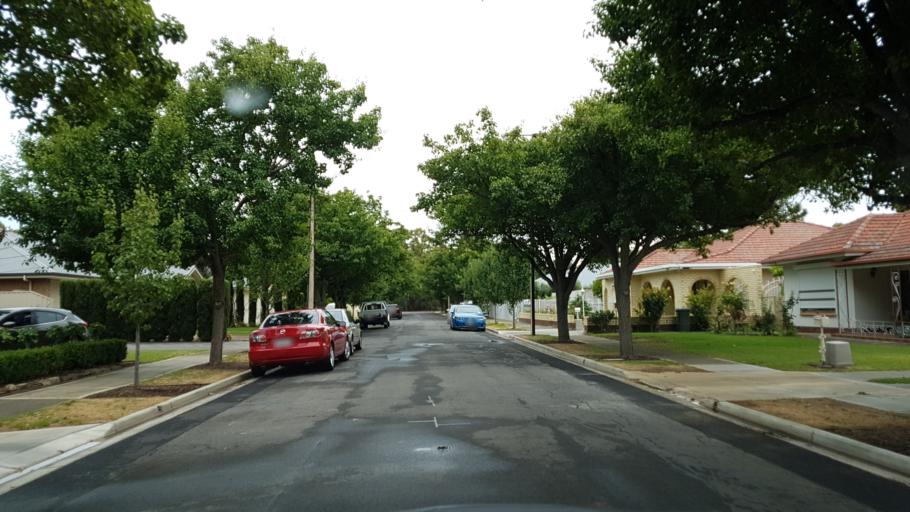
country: AU
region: South Australia
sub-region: Charles Sturt
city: Seaton
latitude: -34.9247
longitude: 138.5197
